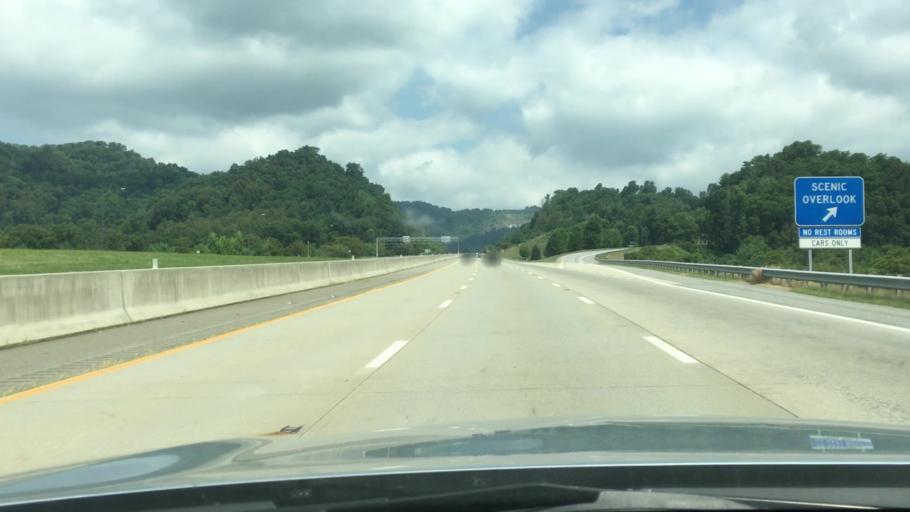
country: US
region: North Carolina
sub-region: Madison County
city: Mars Hill
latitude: 35.8624
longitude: -82.5323
